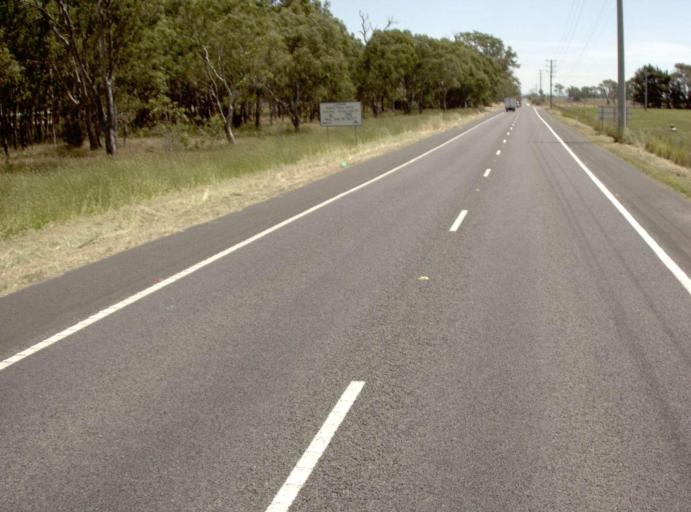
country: AU
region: Victoria
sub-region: Latrobe
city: Traralgon
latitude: -38.1734
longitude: 146.6618
